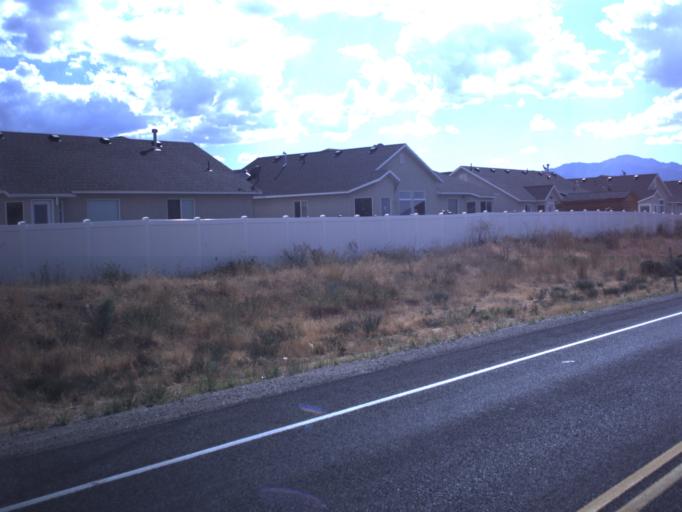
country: US
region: Utah
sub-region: Tooele County
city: Tooele
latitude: 40.5510
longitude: -112.3062
